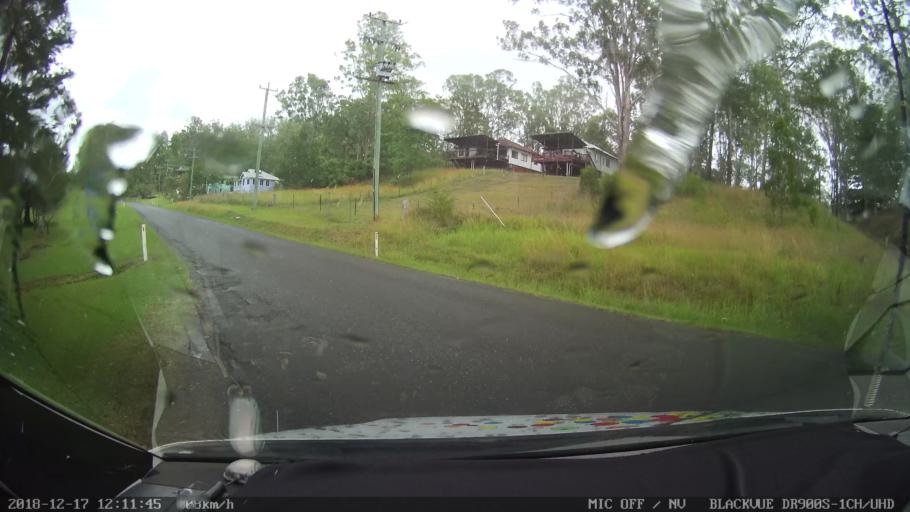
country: AU
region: New South Wales
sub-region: Kyogle
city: Kyogle
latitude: -28.4683
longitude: 152.5483
